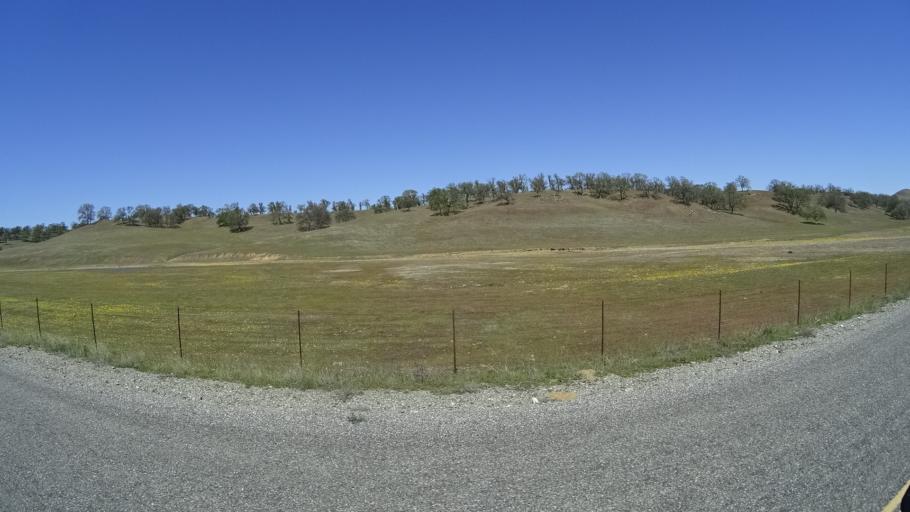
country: US
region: California
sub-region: Glenn County
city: Orland
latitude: 39.7565
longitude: -122.3522
